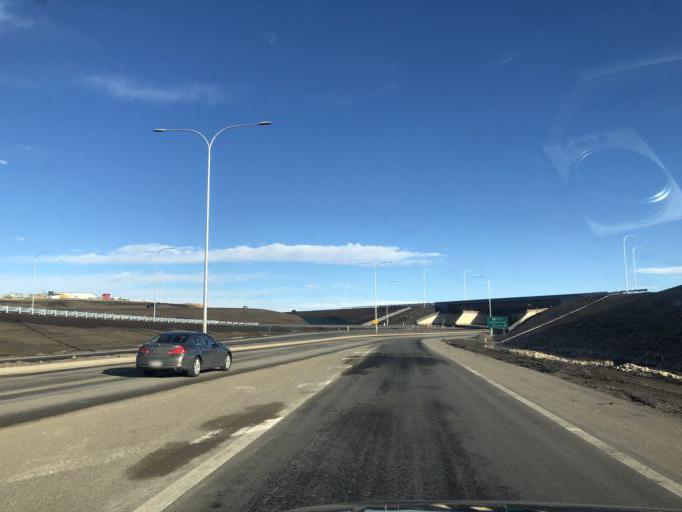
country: CA
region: Alberta
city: Calgary
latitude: 50.9501
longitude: -114.1434
